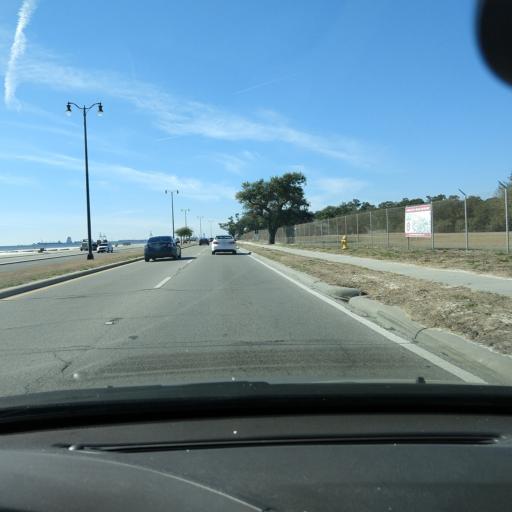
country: US
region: Mississippi
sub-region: Harrison County
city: Gulfport
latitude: 30.3763
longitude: -89.0526
